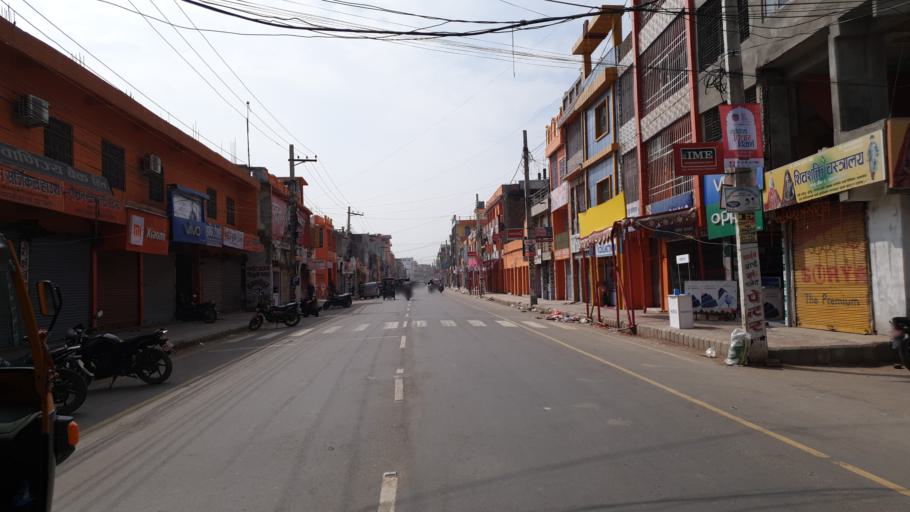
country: NP
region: Central Region
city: Janakpur
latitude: 26.7316
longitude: 85.9327
